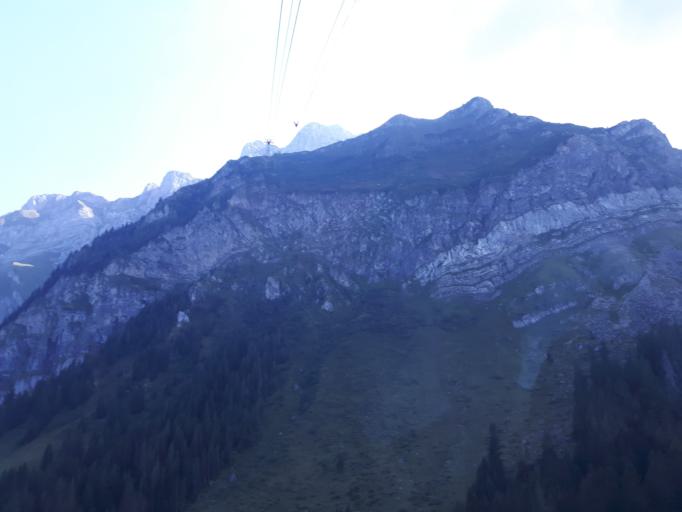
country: CH
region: Lucerne
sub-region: Lucerne-Land District
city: Kriens
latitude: 46.9899
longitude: 8.2517
